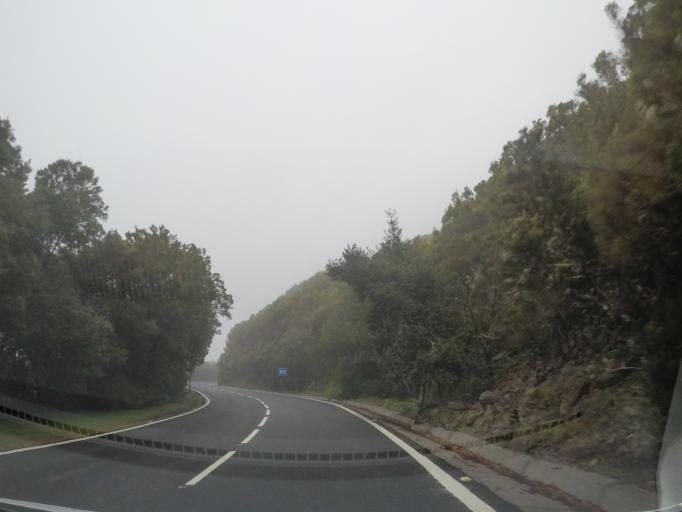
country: ES
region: Canary Islands
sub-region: Provincia de Santa Cruz de Tenerife
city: Alajero
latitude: 28.1143
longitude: -17.2427
